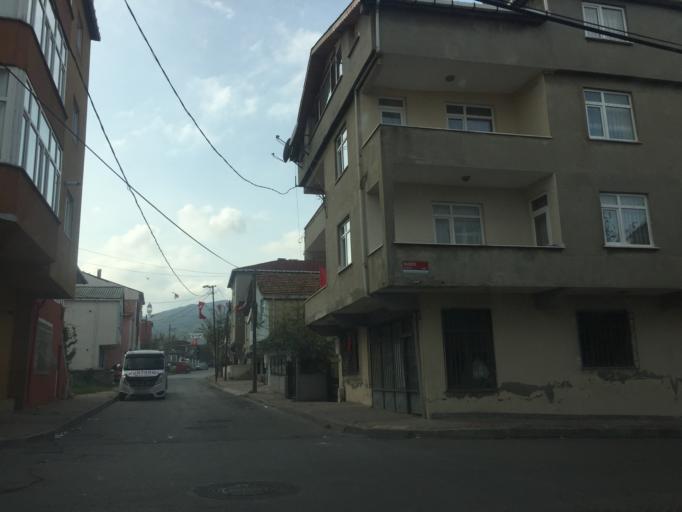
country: TR
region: Istanbul
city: Sultanbeyli
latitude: 40.9367
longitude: 29.2866
